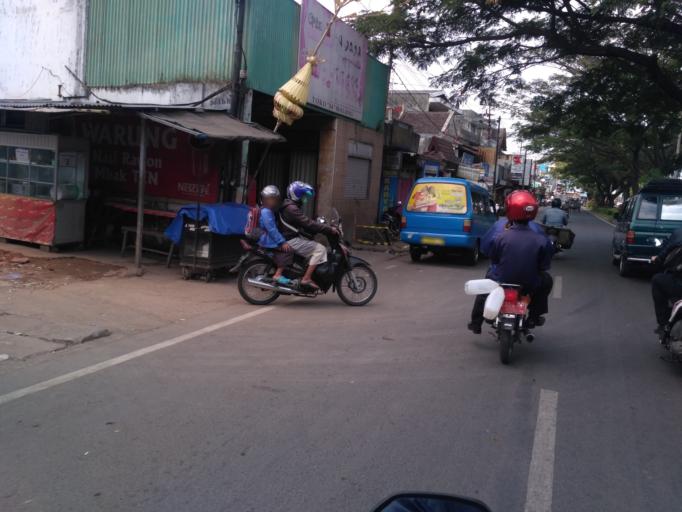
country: ID
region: East Java
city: Malang
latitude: -7.9409
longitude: 112.6402
